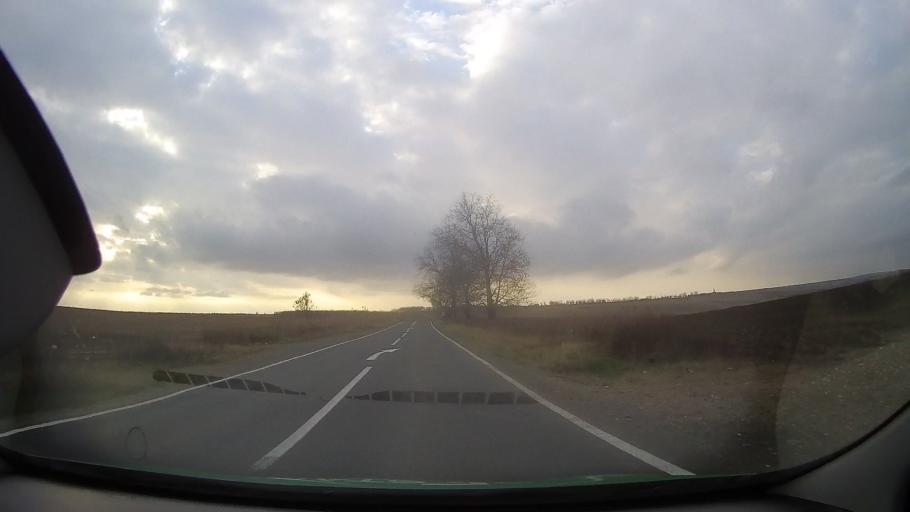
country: RO
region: Constanta
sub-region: Comuna Deleni
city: Deleni
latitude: 44.0886
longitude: 27.9843
